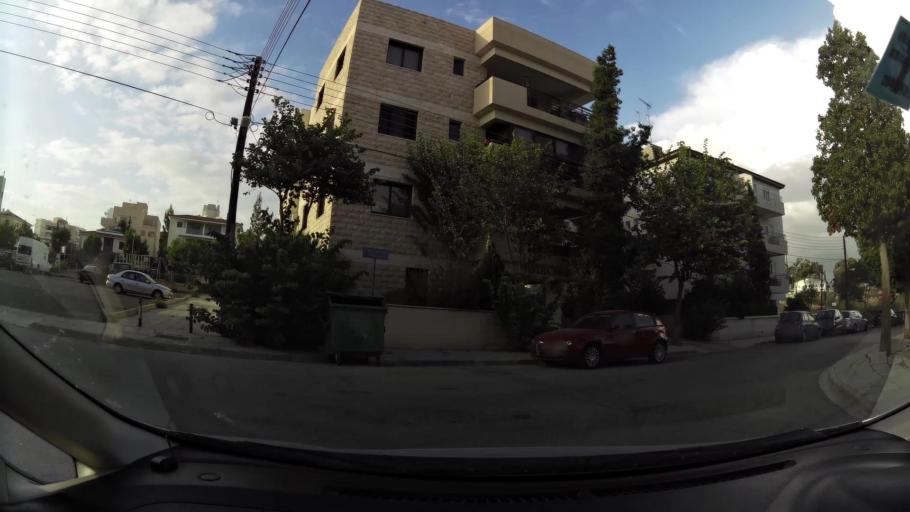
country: CY
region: Lefkosia
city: Nicosia
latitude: 35.1659
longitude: 33.3836
